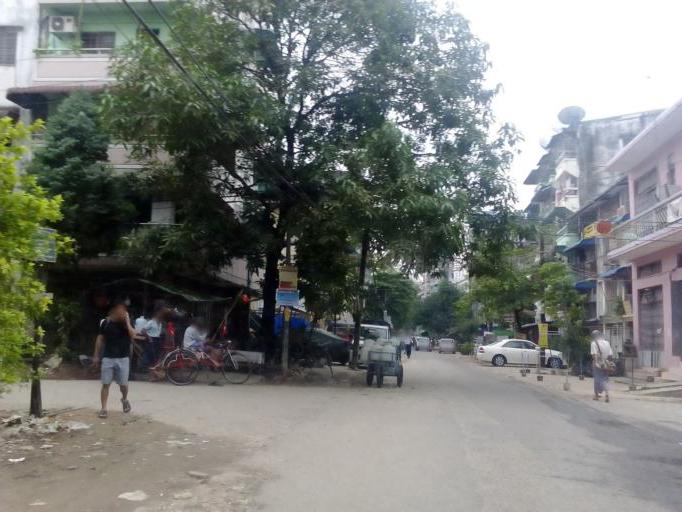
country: MM
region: Yangon
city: Yangon
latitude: 16.8007
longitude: 96.1774
